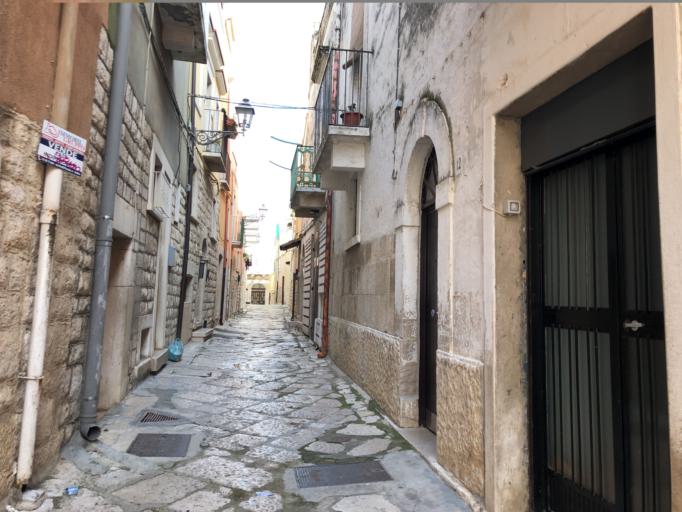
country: IT
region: Apulia
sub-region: Provincia di Barletta - Andria - Trani
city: Andria
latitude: 41.2265
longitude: 16.2958
